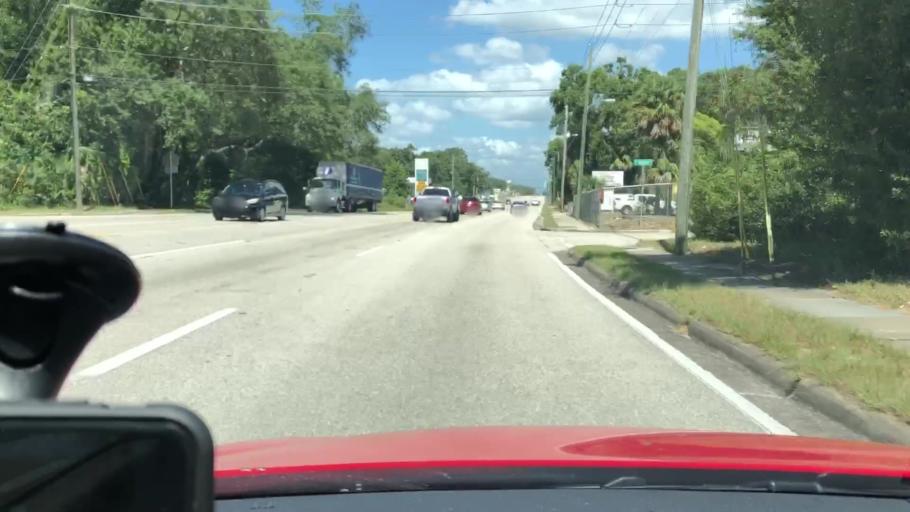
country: US
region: Florida
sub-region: Volusia County
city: West DeLand
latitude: 29.0151
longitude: -81.3238
